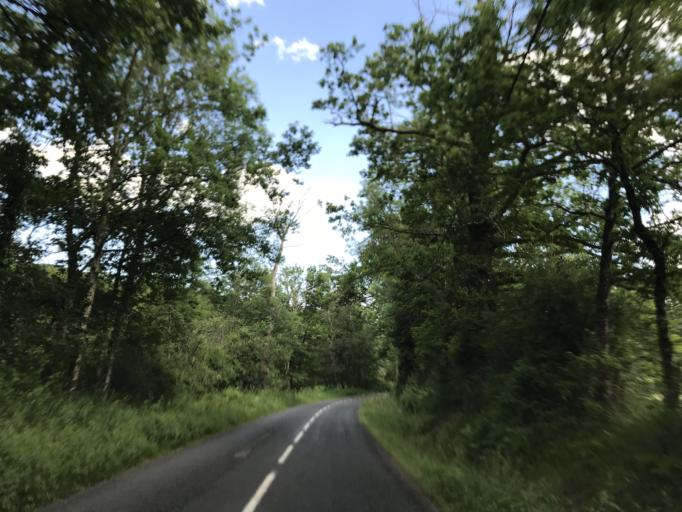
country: FR
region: Auvergne
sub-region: Departement du Puy-de-Dome
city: Courpiere
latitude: 45.7707
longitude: 3.5995
